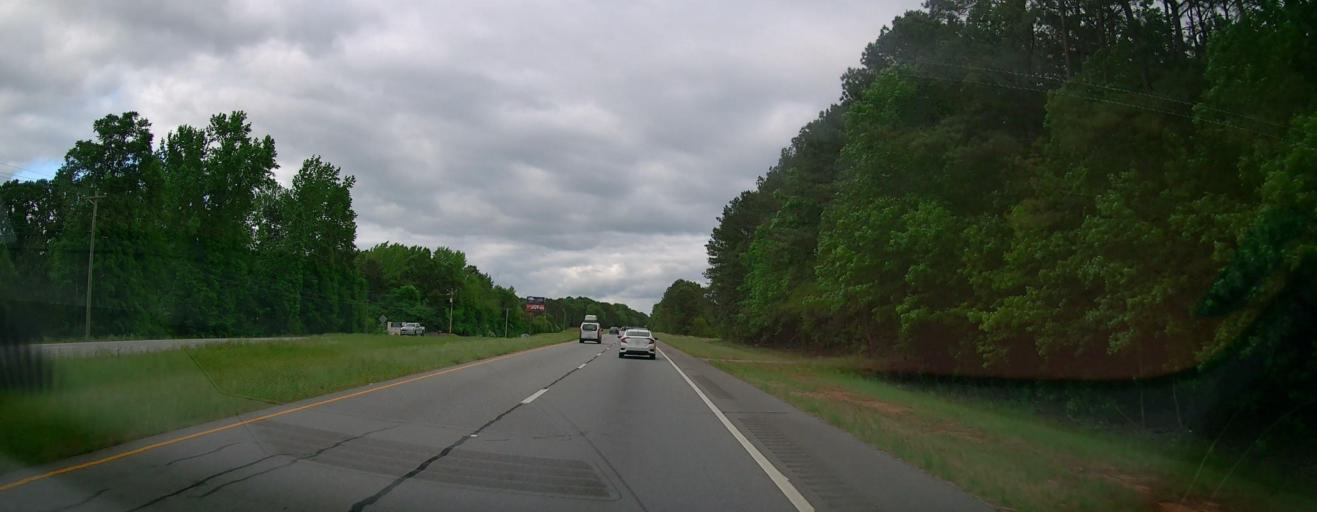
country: US
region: Georgia
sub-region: Walton County
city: Monroe
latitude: 33.8248
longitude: -83.6620
